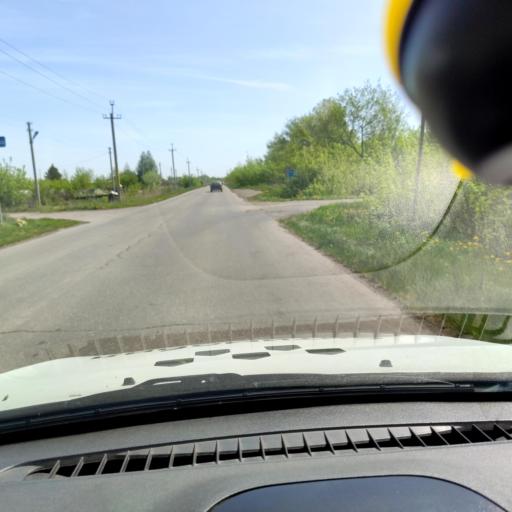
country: RU
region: Samara
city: Tol'yatti
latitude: 53.6644
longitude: 49.3475
